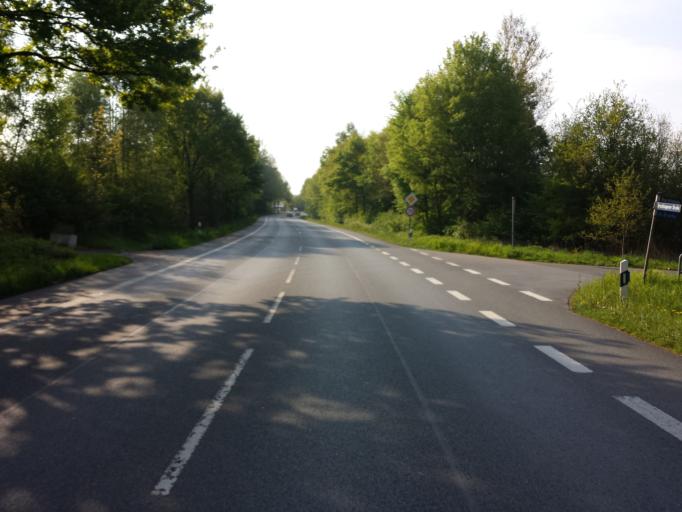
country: DE
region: North Rhine-Westphalia
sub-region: Regierungsbezirk Detmold
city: Guetersloh
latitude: 51.9498
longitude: 8.3446
